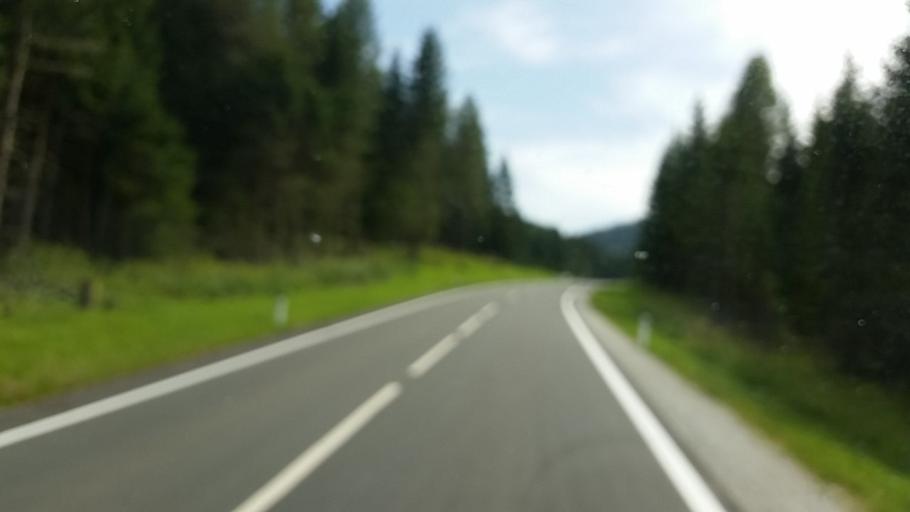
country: AT
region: Salzburg
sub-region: Politischer Bezirk Tamsweg
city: Sankt Michael im Lungau
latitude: 47.0748
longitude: 13.6177
